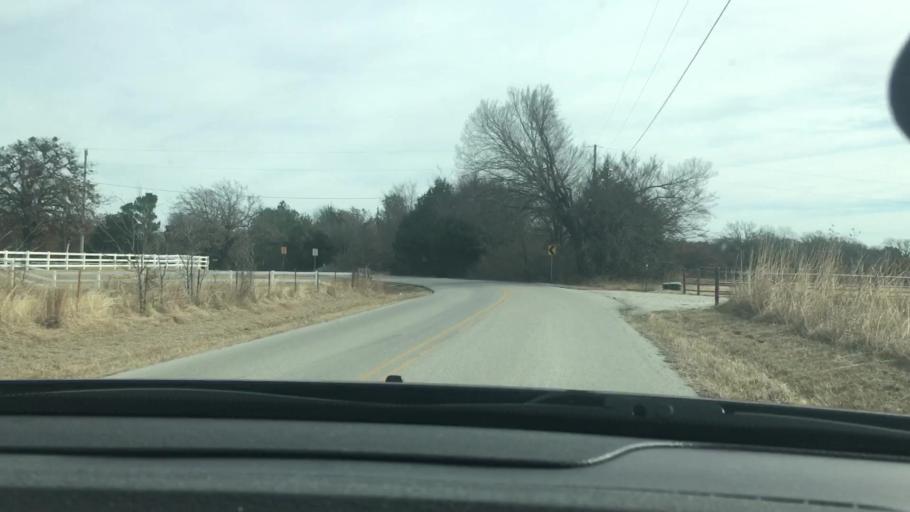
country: US
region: Oklahoma
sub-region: Carter County
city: Ardmore
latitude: 34.1729
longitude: -97.0793
